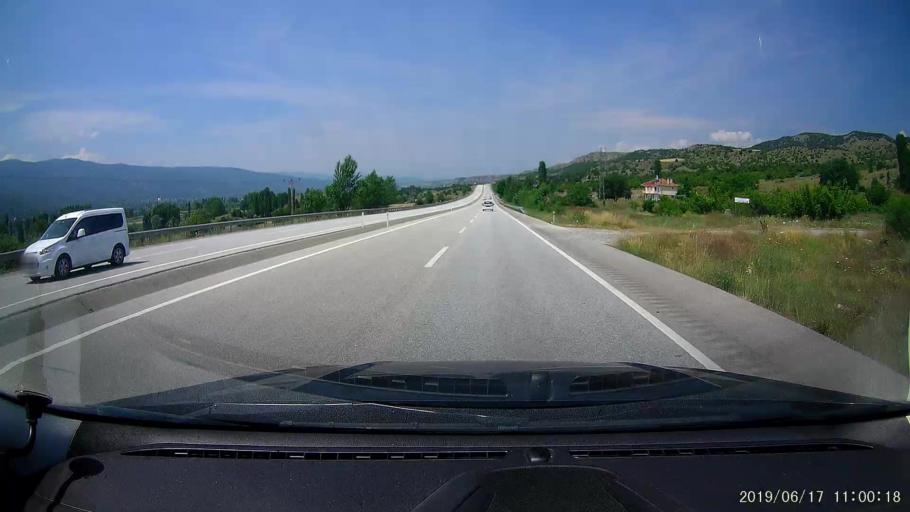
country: TR
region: Kastamonu
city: Tosya
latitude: 41.0355
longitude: 34.1837
